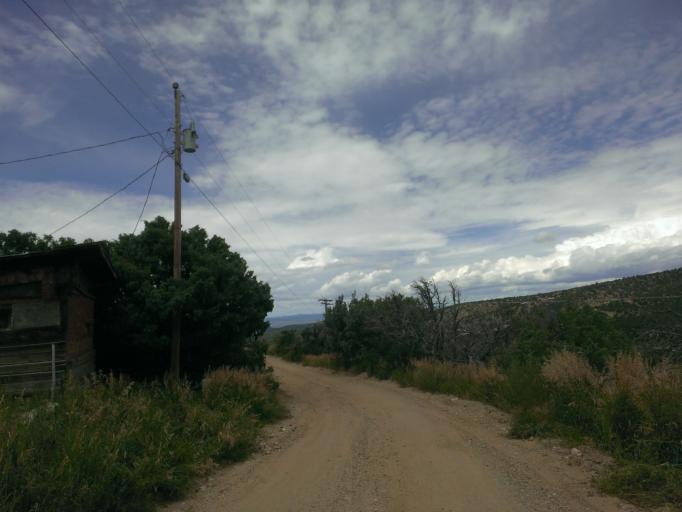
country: US
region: New Mexico
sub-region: Taos County
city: Arroyo Seco
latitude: 36.5346
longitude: -105.5608
